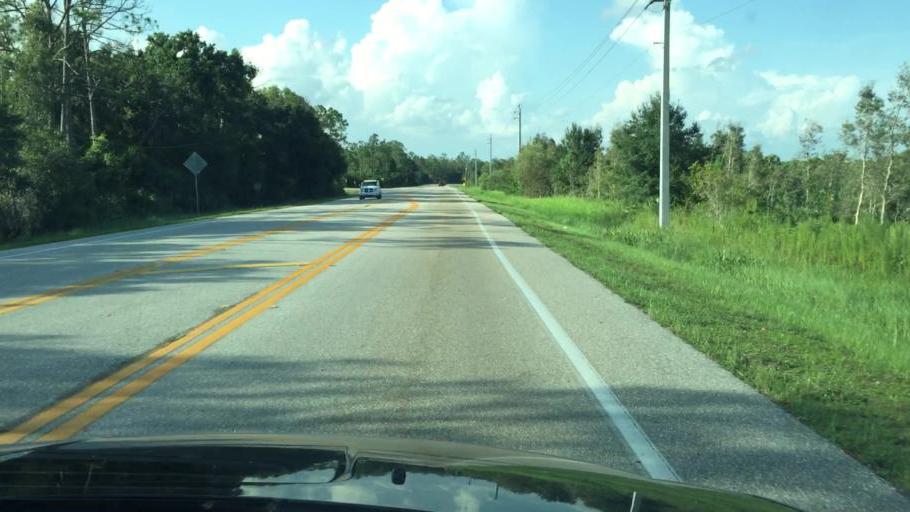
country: US
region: Florida
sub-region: Lee County
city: Buckingham
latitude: 26.6295
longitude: -81.7567
